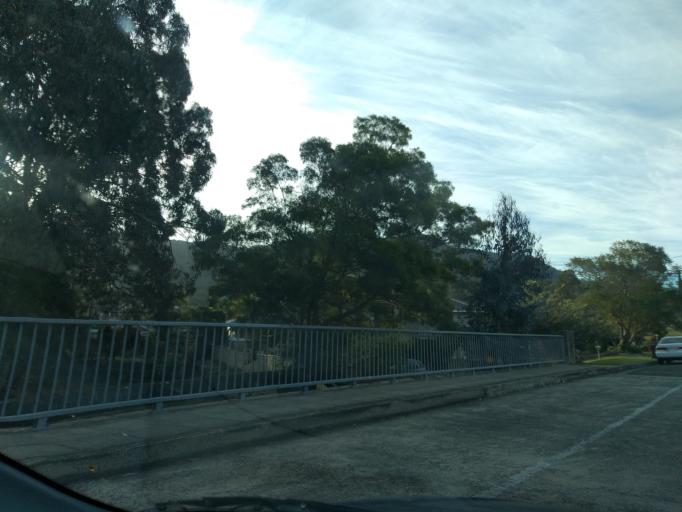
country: AU
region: New South Wales
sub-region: Wollongong
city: Mount Ousley
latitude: -34.3863
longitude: 150.8812
